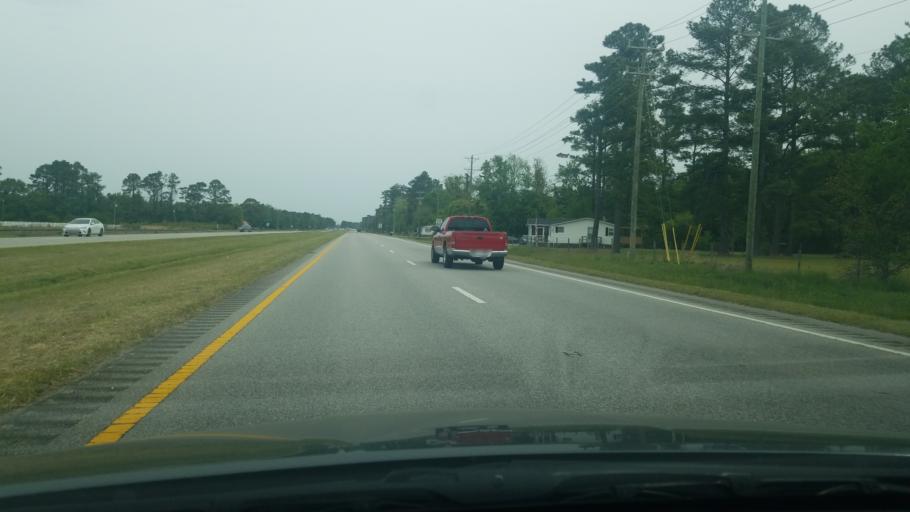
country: US
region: North Carolina
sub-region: Beaufort County
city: Washington
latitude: 35.4551
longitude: -77.1221
